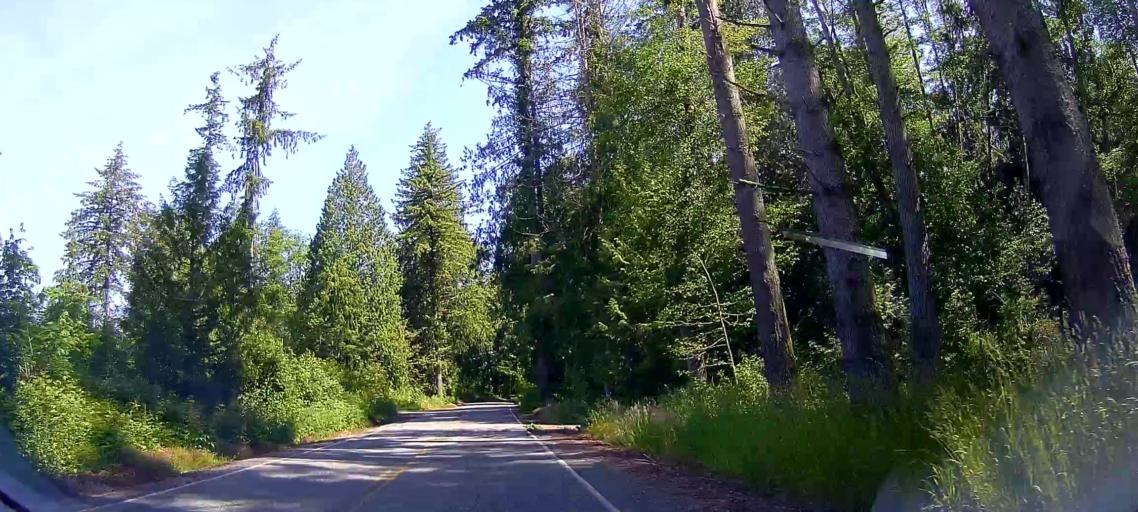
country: US
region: Washington
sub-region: Skagit County
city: Burlington
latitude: 48.5483
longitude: -122.3108
